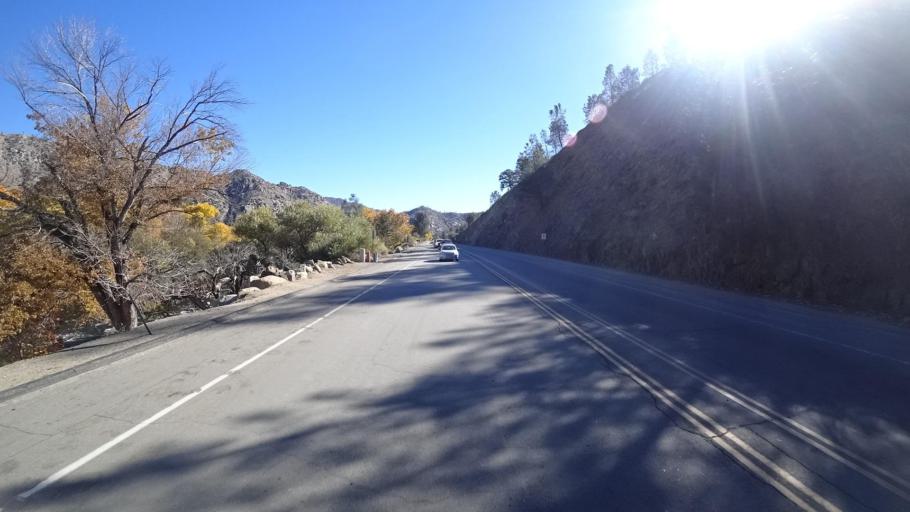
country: US
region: California
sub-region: Kern County
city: Kernville
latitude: 35.7516
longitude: -118.4234
